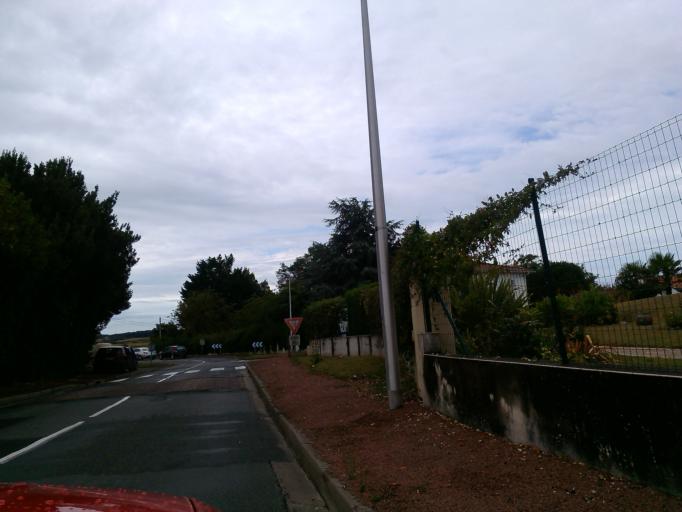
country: FR
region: Poitou-Charentes
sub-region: Departement de la Charente-Maritime
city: Arvert
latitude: 45.7396
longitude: -1.1291
